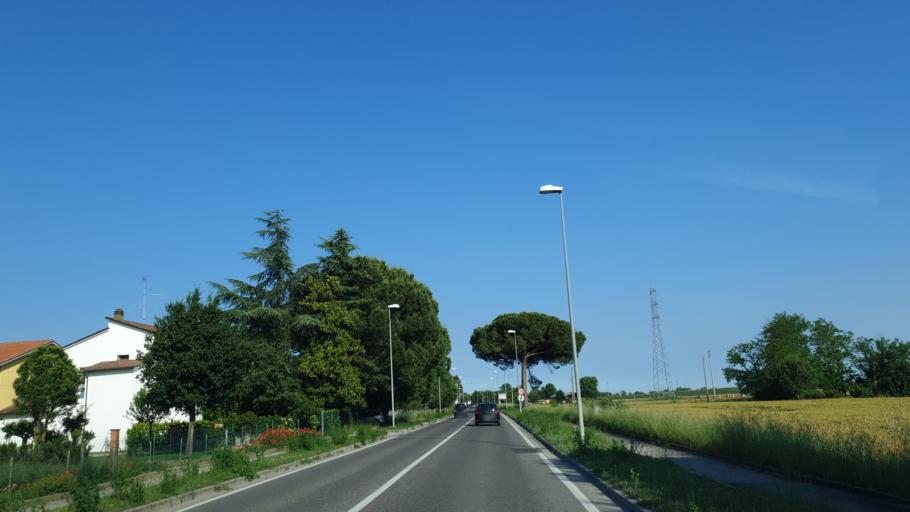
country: IT
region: Emilia-Romagna
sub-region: Provincia di Ravenna
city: Porto Fuori
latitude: 44.4085
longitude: 12.2340
